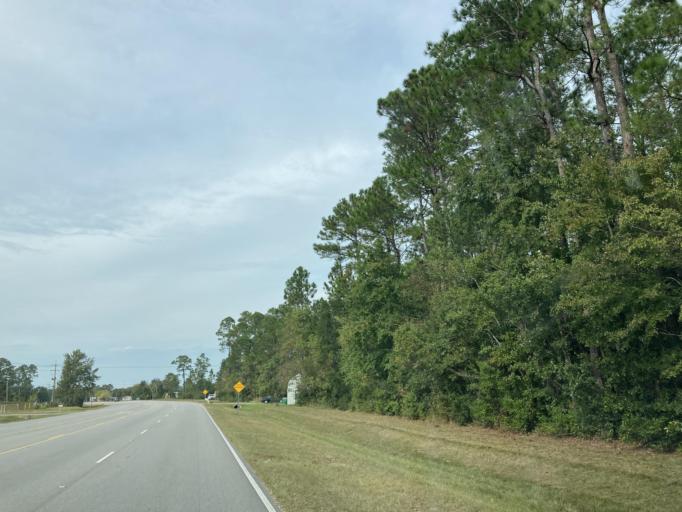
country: US
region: Mississippi
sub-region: Jackson County
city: Saint Martin
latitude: 30.4772
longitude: -88.8498
